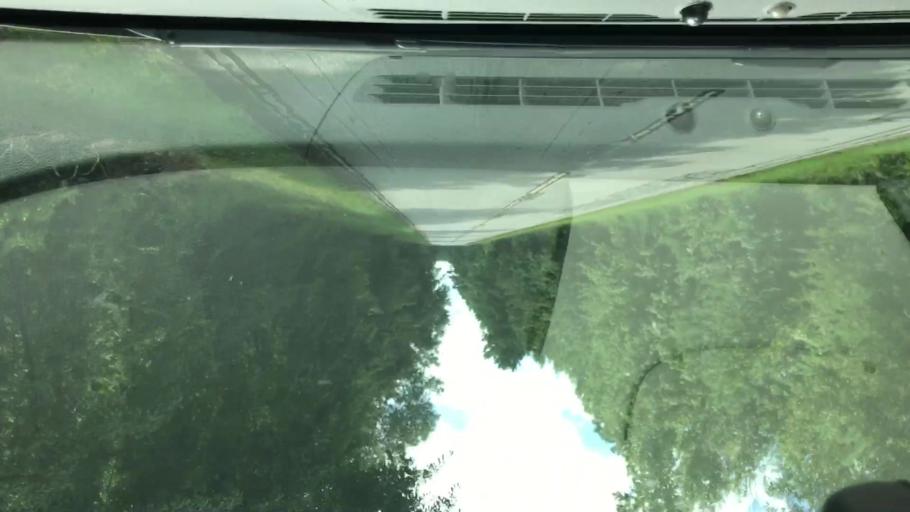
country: US
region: Georgia
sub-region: Quitman County
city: Georgetown
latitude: 32.0345
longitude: -85.0266
